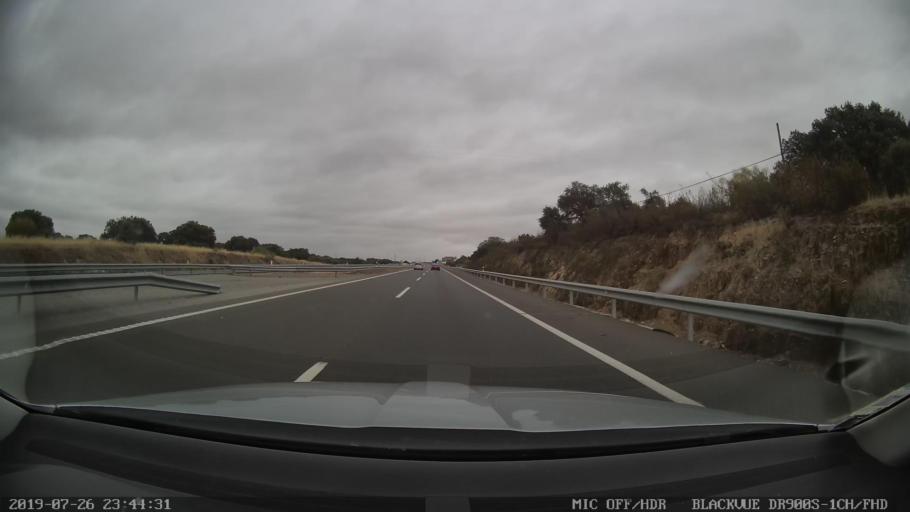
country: ES
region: Extremadura
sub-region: Provincia de Caceres
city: Torrecillas de la Tiesa
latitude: 39.5497
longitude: -5.8332
